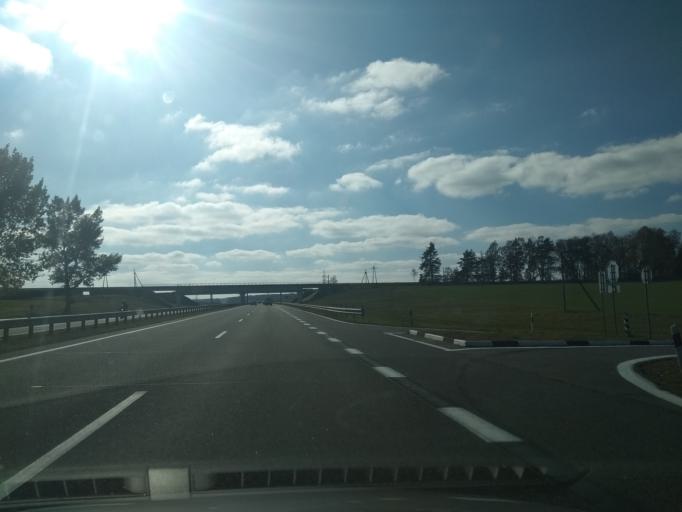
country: BY
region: Brest
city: Baranovichi
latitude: 53.1127
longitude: 25.8931
